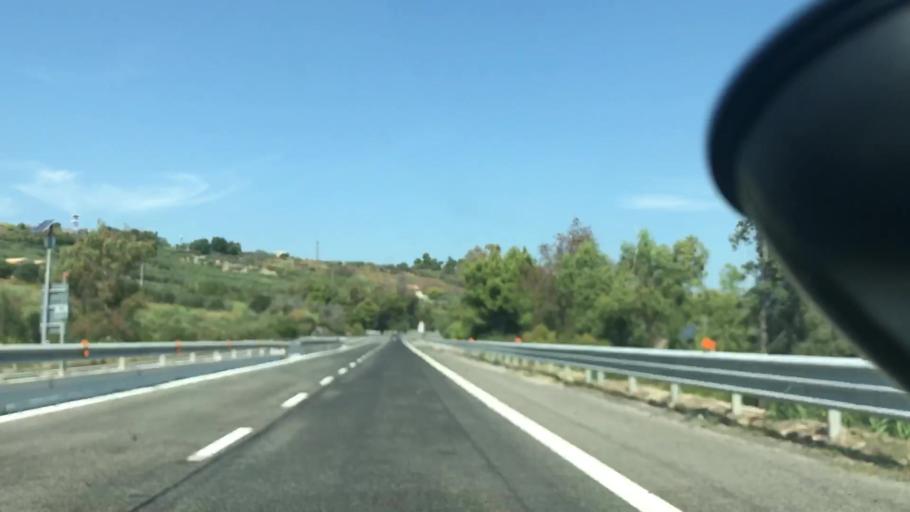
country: IT
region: Abruzzo
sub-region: Provincia di Chieti
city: Marina di Vasto
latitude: 42.0812
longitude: 14.7013
